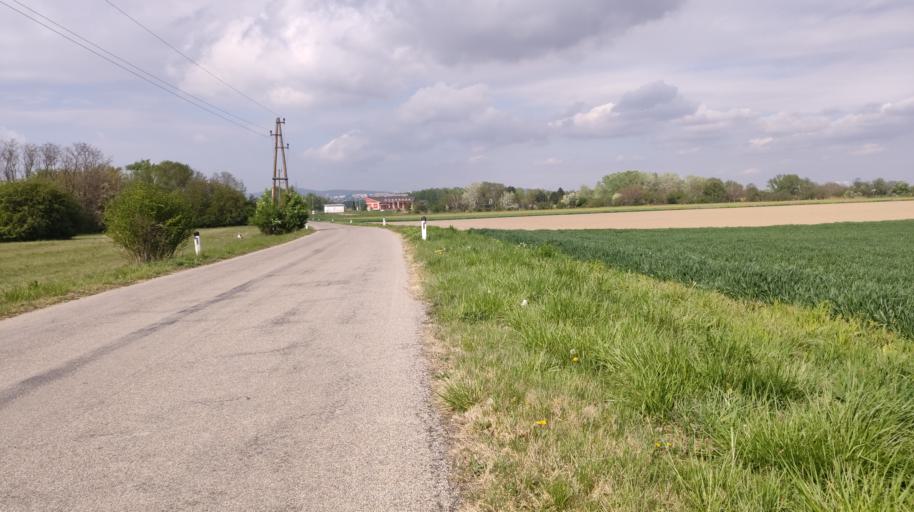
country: AT
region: Burgenland
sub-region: Politischer Bezirk Neusiedl am See
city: Kittsee
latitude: 48.1186
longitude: 17.0598
